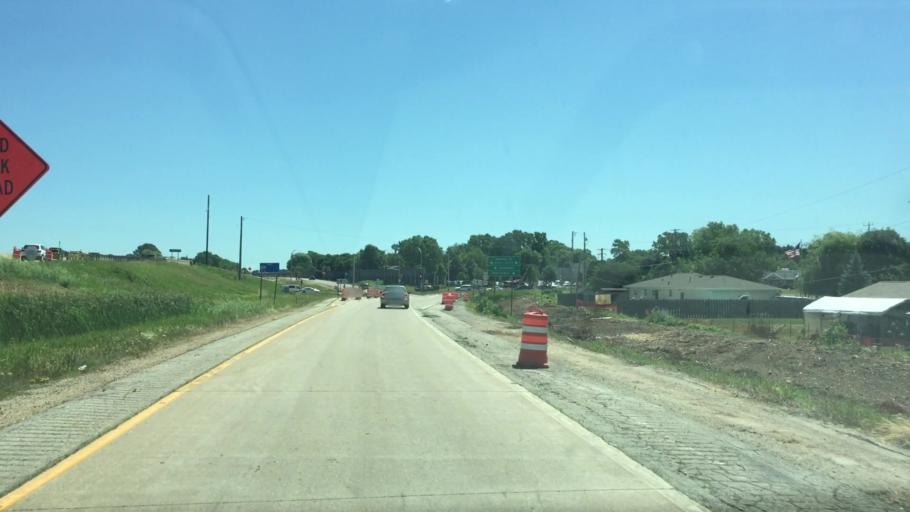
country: US
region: Wisconsin
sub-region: Outagamie County
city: Appleton
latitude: 44.2334
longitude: -88.4067
